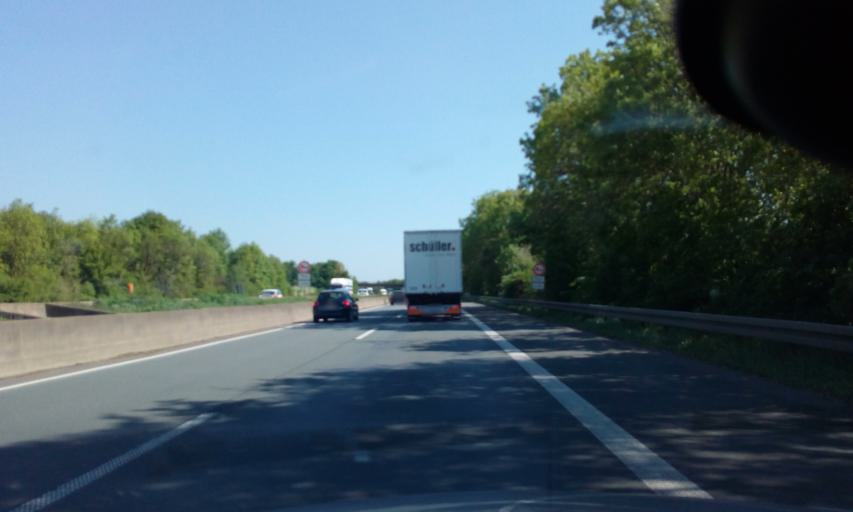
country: DE
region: North Rhine-Westphalia
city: Tuernich
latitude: 50.8535
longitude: 6.7257
